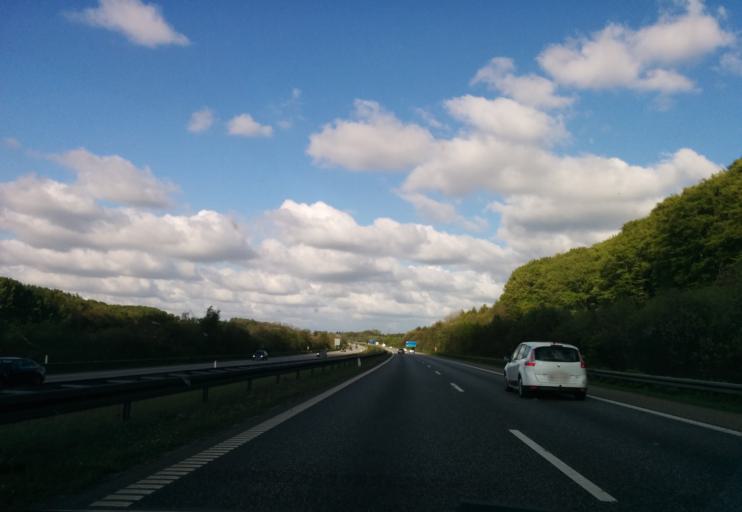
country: DK
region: Central Jutland
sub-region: Skanderborg Kommune
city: Skanderborg
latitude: 56.0558
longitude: 9.9514
